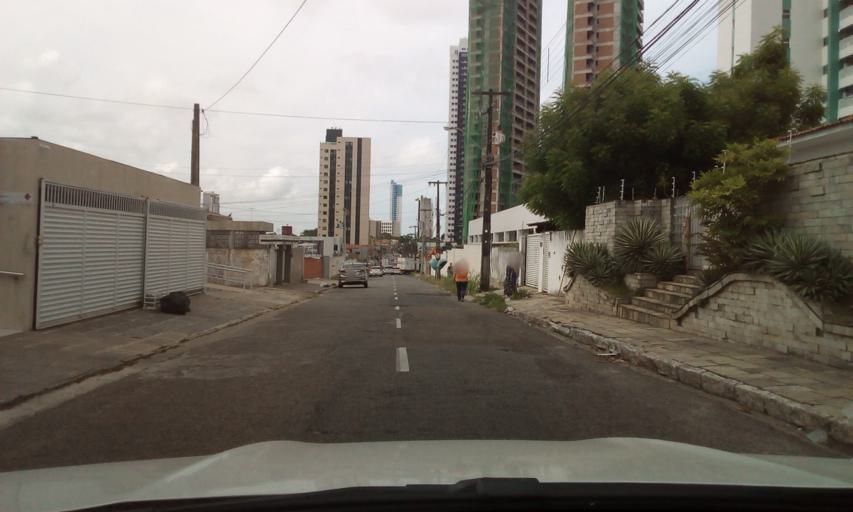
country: BR
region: Paraiba
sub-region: Joao Pessoa
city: Joao Pessoa
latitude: -7.1162
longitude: -34.8408
